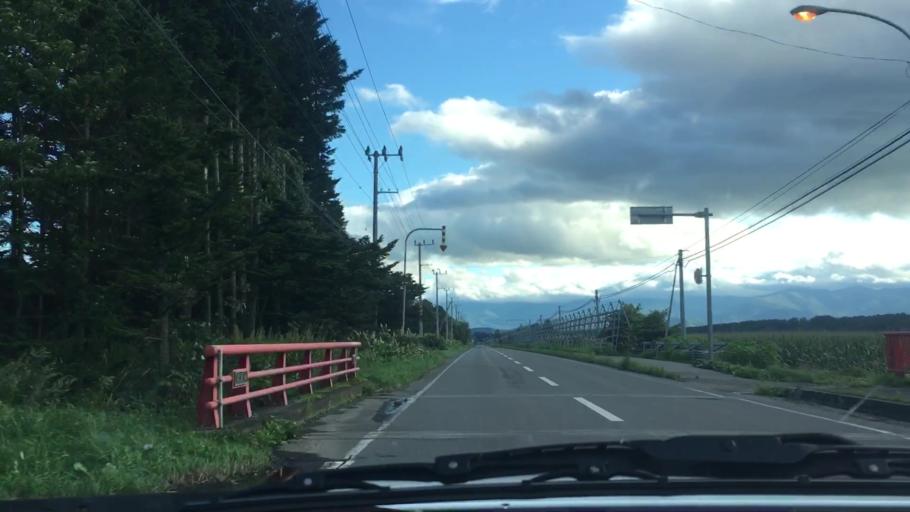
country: JP
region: Hokkaido
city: Otofuke
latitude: 43.1441
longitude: 142.8973
